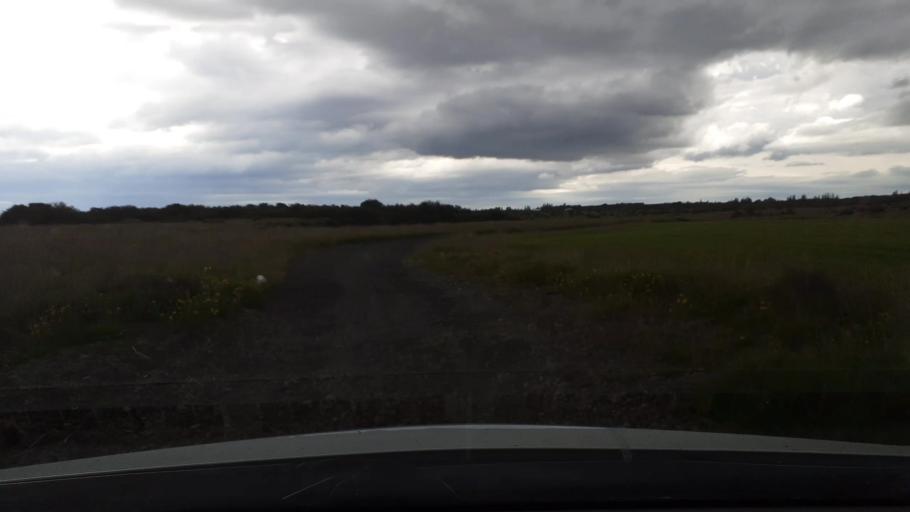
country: IS
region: West
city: Borgarnes
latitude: 64.6388
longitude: -21.7413
